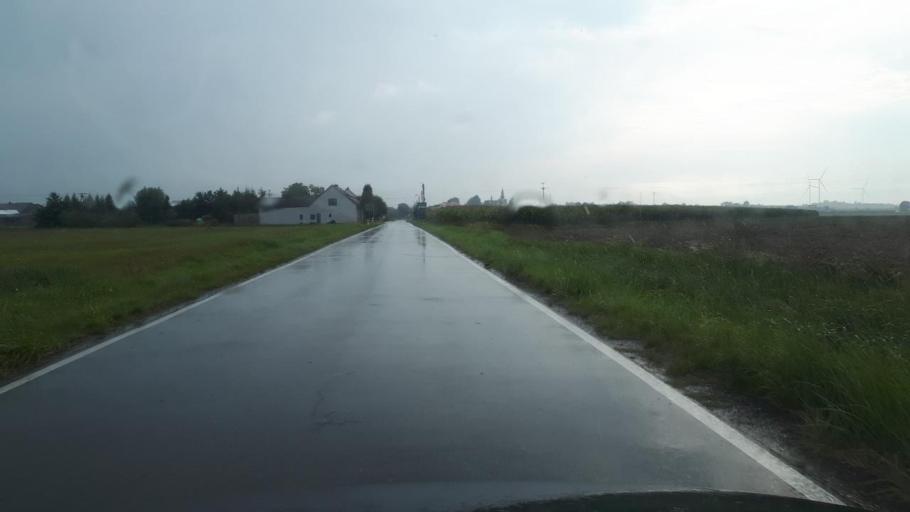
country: PL
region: Silesian Voivodeship
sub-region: Powiat gliwicki
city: Wielowies
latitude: 50.5156
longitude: 18.6262
